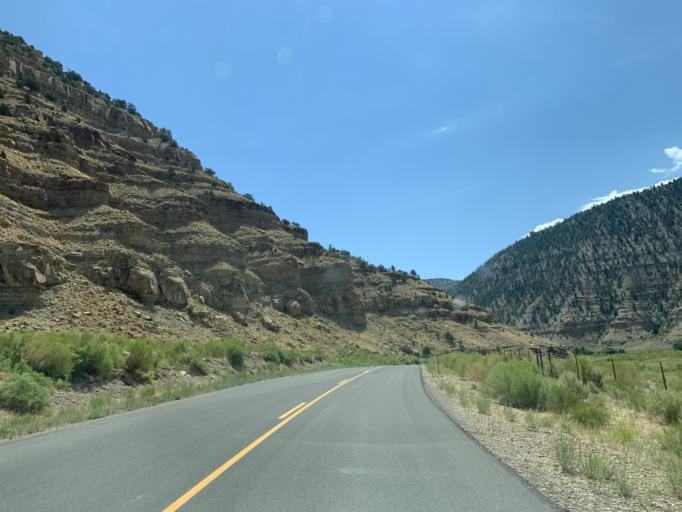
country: US
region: Utah
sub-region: Carbon County
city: East Carbon City
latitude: 39.8048
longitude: -110.3737
